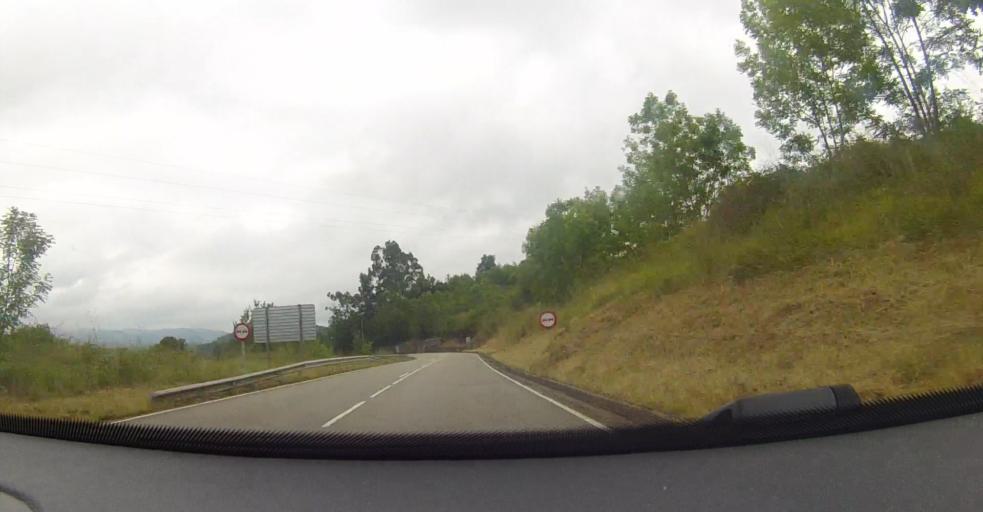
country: ES
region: Asturias
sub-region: Province of Asturias
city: Villaviciosa
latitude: 43.4938
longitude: -5.4326
